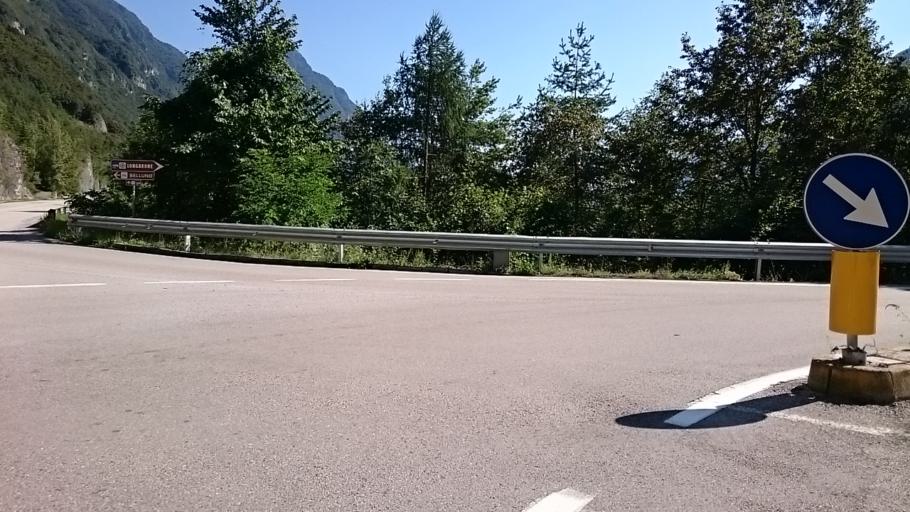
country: IT
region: Veneto
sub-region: Provincia di Belluno
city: Longarone
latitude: 46.2680
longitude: 12.3109
